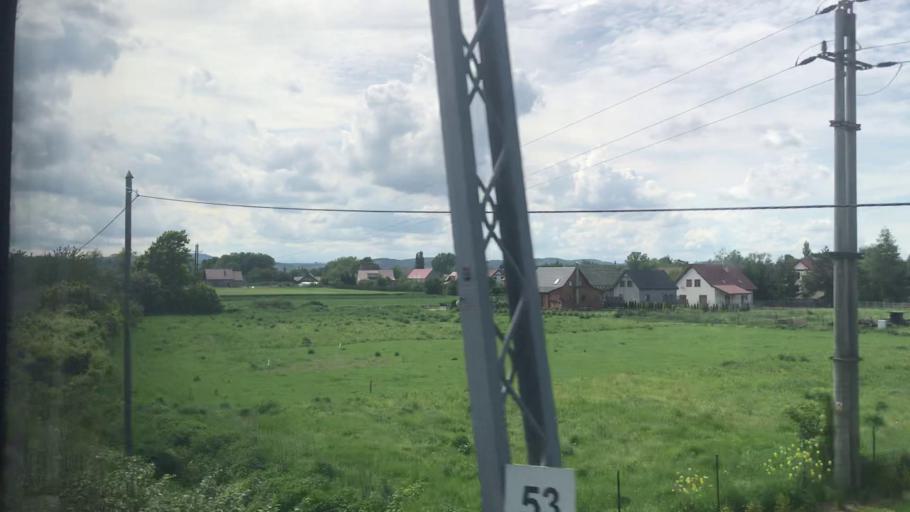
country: PL
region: Lower Silesian Voivodeship
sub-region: Powiat swidnicki
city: Stanowice
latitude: 50.8792
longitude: 16.3777
